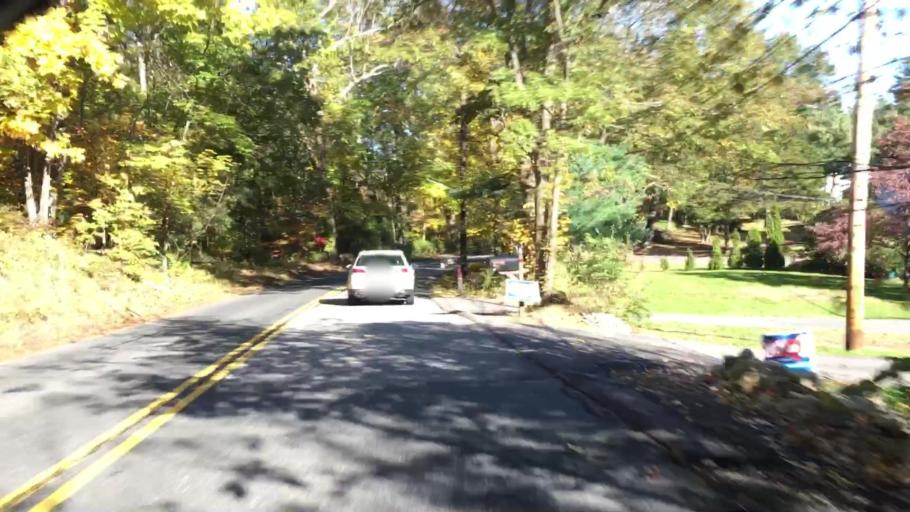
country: US
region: Massachusetts
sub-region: Middlesex County
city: Ashland
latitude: 42.2801
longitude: -71.4609
